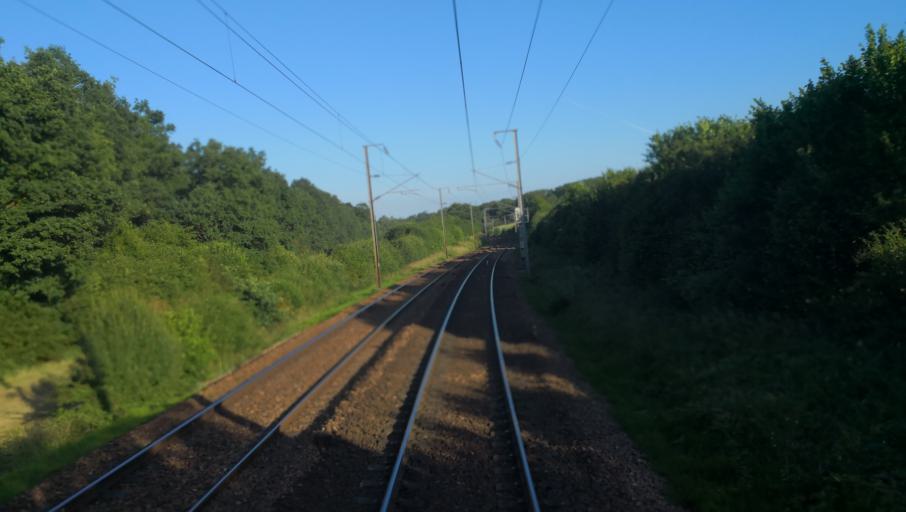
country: FR
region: Haute-Normandie
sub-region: Departement de l'Eure
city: Bernay
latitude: 49.0903
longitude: 0.5628
